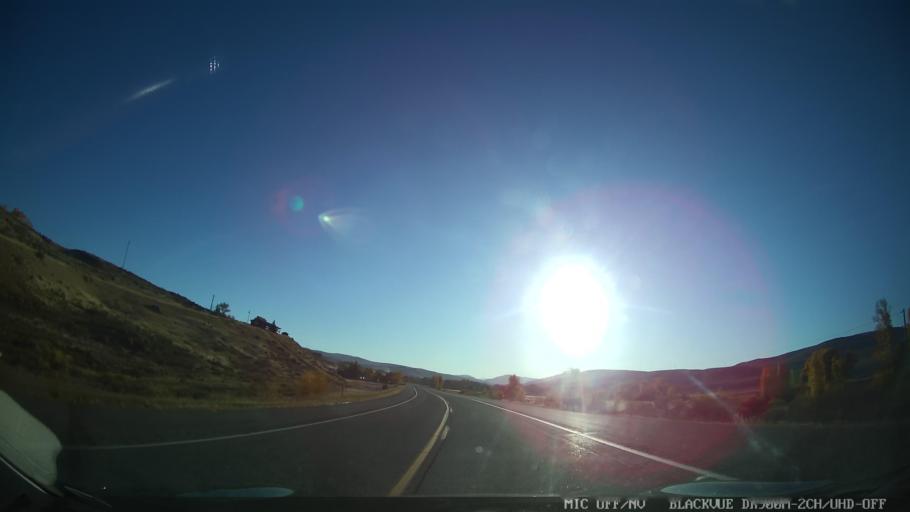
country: US
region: Colorado
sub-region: Grand County
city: Kremmling
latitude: 40.0629
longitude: -106.2494
